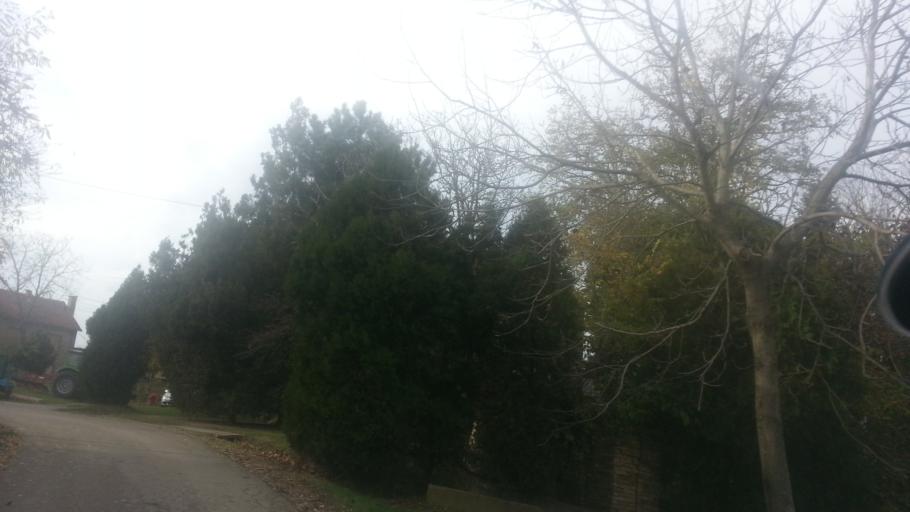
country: RS
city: Putinci
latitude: 44.9959
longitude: 19.9713
